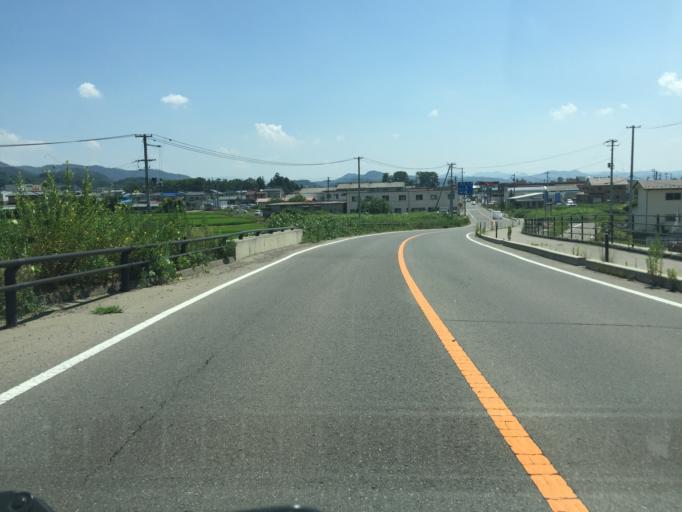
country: JP
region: Fukushima
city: Yanagawamachi-saiwaicho
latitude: 37.8669
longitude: 140.6088
